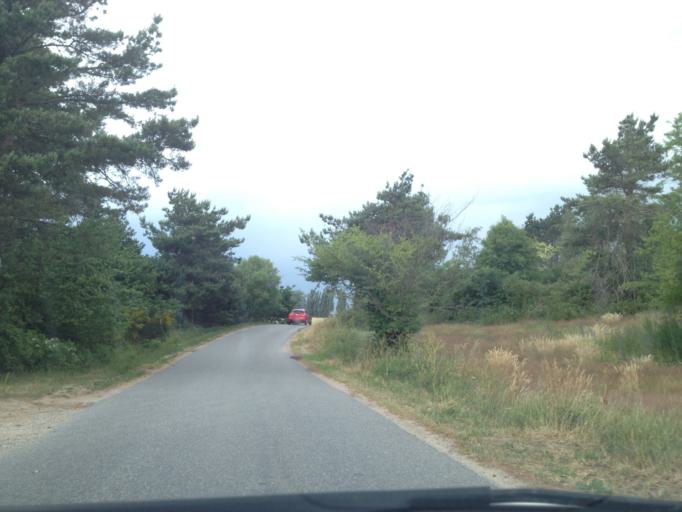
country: DK
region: Central Jutland
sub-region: Syddjurs Kommune
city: Ebeltoft
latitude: 56.1673
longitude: 10.6776
